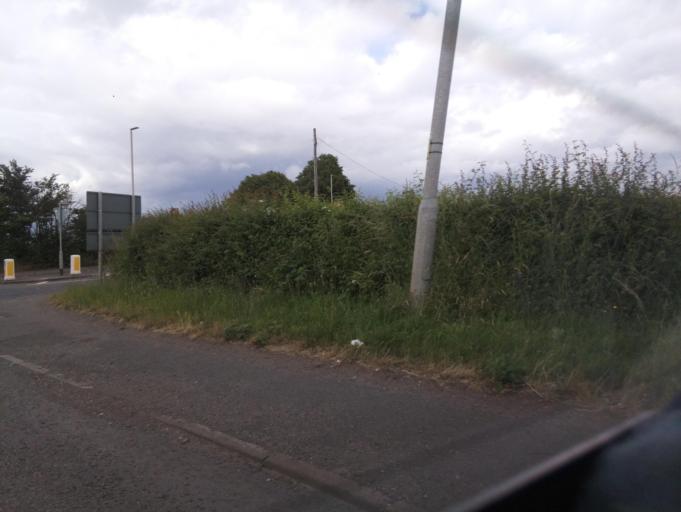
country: GB
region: England
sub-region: Dudley
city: Kingswinford
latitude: 52.4945
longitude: -2.1885
